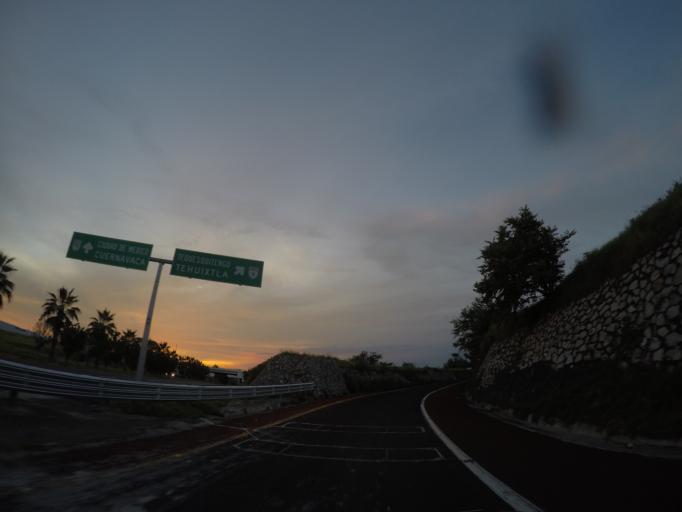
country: MX
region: Morelos
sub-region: Jojutla
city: Tehuixtla
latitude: 18.5878
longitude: -99.2582
